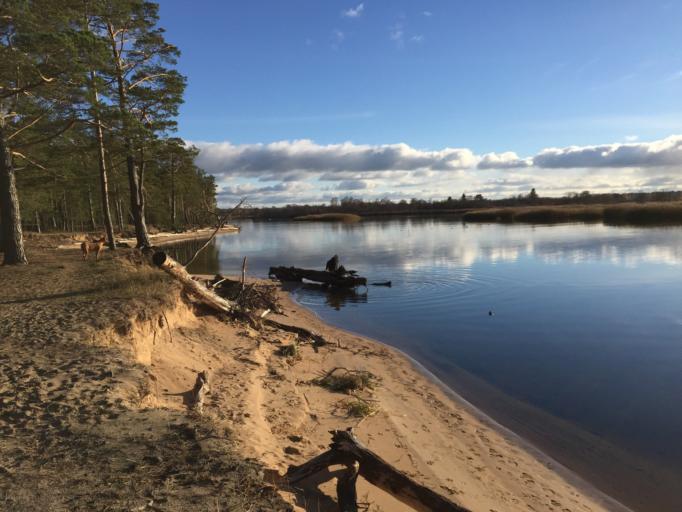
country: LV
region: Carnikava
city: Carnikava
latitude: 57.1576
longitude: 24.2720
